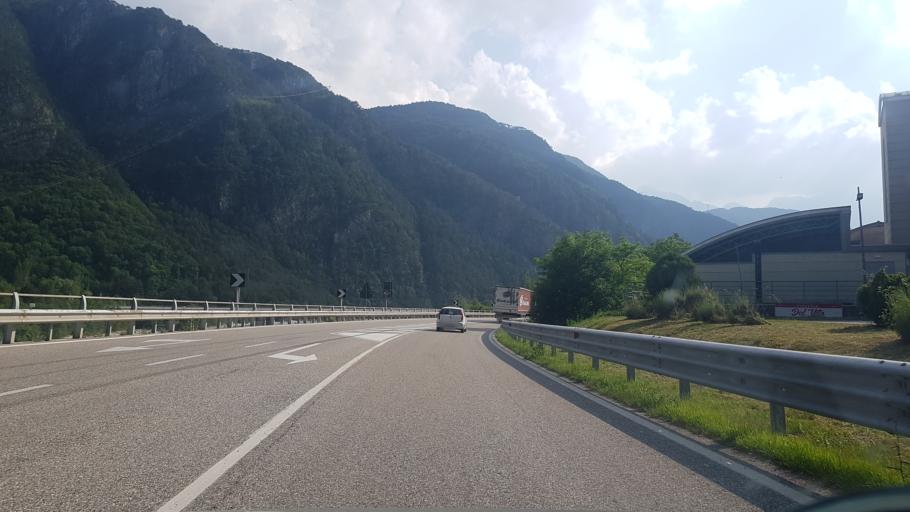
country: IT
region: Friuli Venezia Giulia
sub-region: Provincia di Udine
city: Chiusaforte
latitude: 46.4085
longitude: 13.3115
